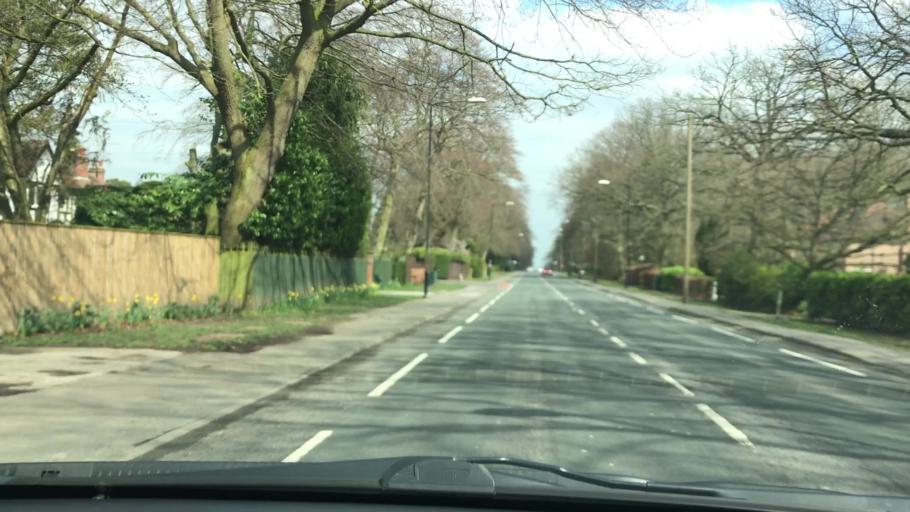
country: GB
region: England
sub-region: North Yorkshire
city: Harrogate
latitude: 53.9859
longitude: -1.5141
